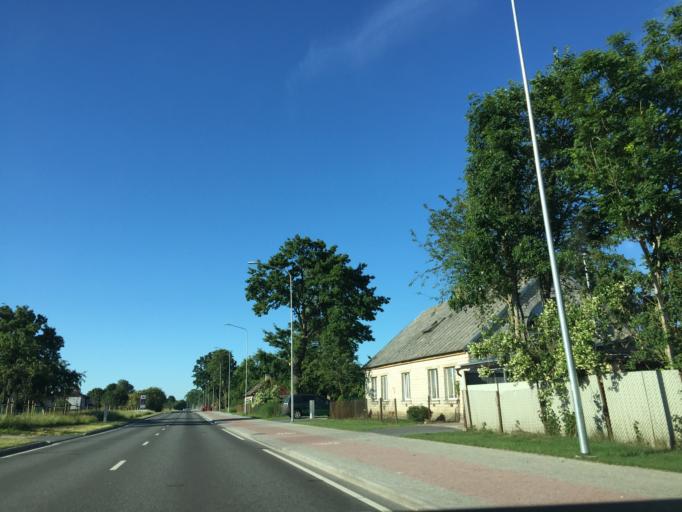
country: LV
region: Ventspils
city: Ventspils
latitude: 57.3812
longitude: 21.6143
